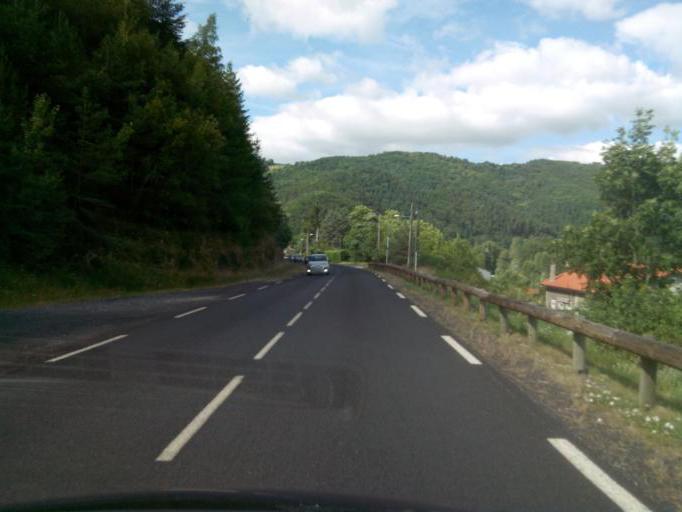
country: FR
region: Auvergne
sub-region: Departement de la Haute-Loire
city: Retournac
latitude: 45.2004
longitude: 3.9768
